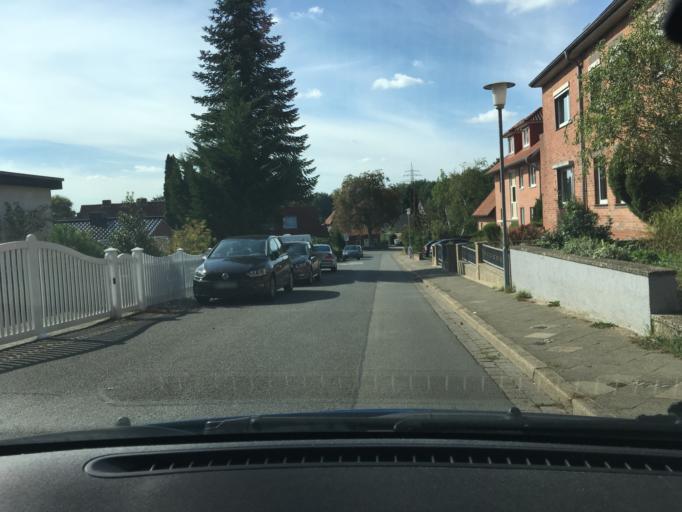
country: DE
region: Lower Saxony
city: Lueneburg
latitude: 53.2277
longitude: 10.3876
